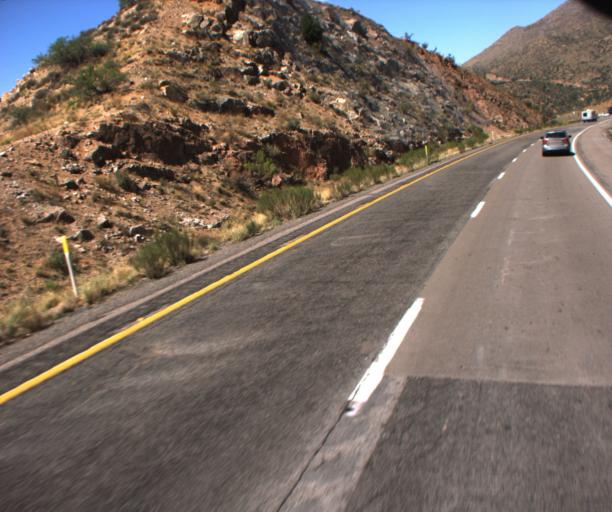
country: US
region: Arizona
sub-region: Mohave County
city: Peach Springs
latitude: 35.1712
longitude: -113.5135
